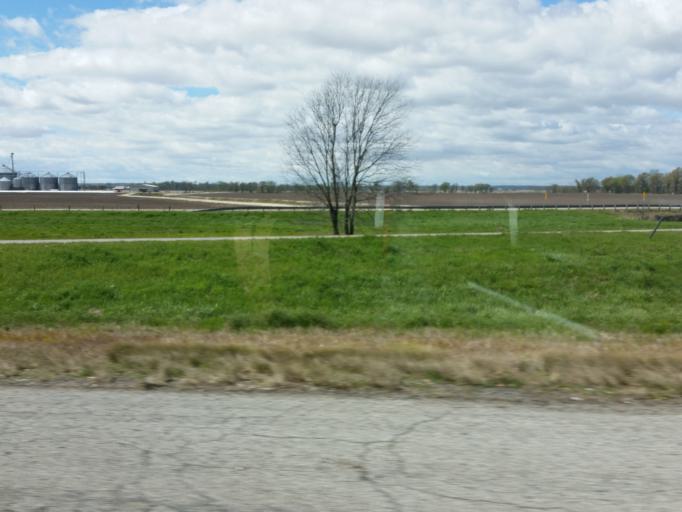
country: US
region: Arkansas
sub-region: Craighead County
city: Bay
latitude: 35.7531
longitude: -90.5795
